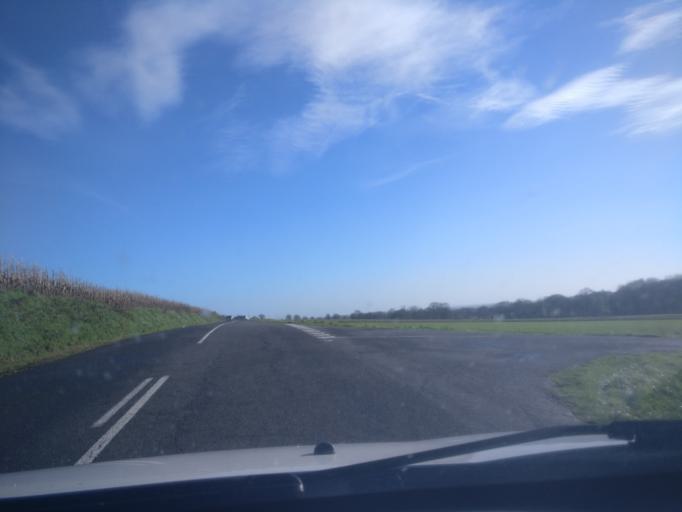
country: FR
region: Brittany
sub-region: Departement d'Ille-et-Vilaine
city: Pleine-Fougeres
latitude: 48.5462
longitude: -1.5970
